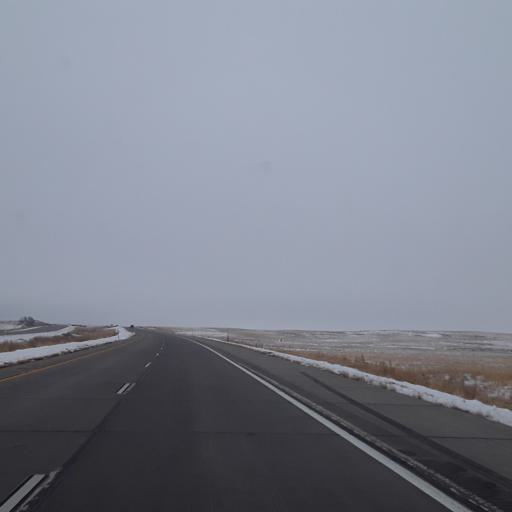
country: US
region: Colorado
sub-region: Logan County
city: Sterling
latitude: 40.5355
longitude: -103.2279
